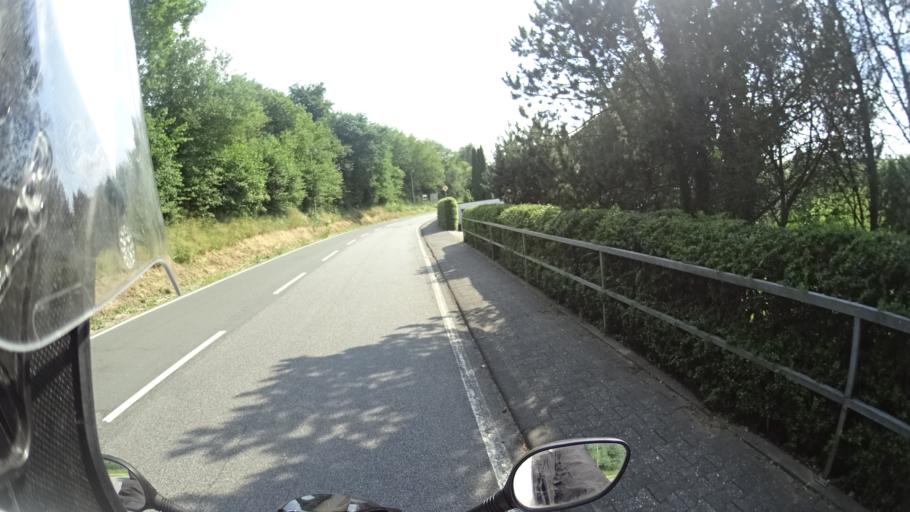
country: DE
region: Hesse
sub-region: Regierungsbezirk Darmstadt
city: Bad Schwalbach
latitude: 50.1321
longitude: 8.0898
